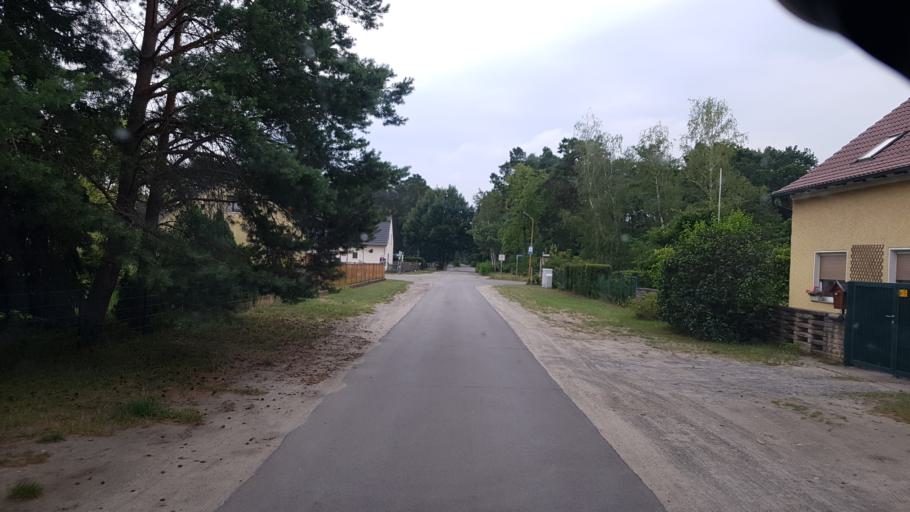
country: DE
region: Brandenburg
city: Gross Koris
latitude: 52.1651
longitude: 13.6937
